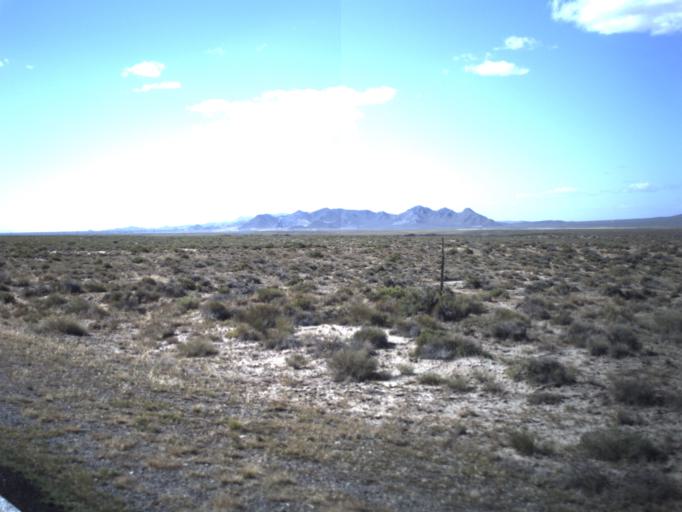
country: US
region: Utah
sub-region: Beaver County
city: Milford
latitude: 38.5422
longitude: -112.9912
